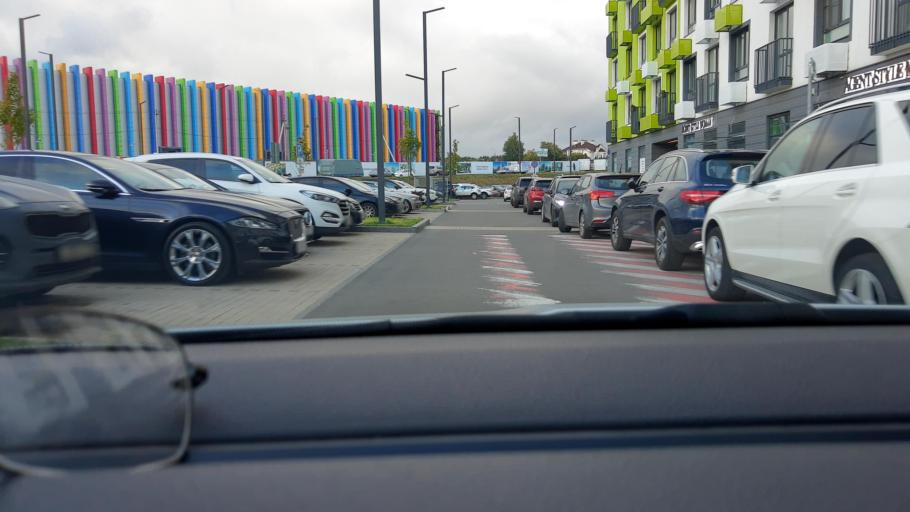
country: RU
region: Moskovskaya
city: Opalikha
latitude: 55.7761
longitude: 37.2399
